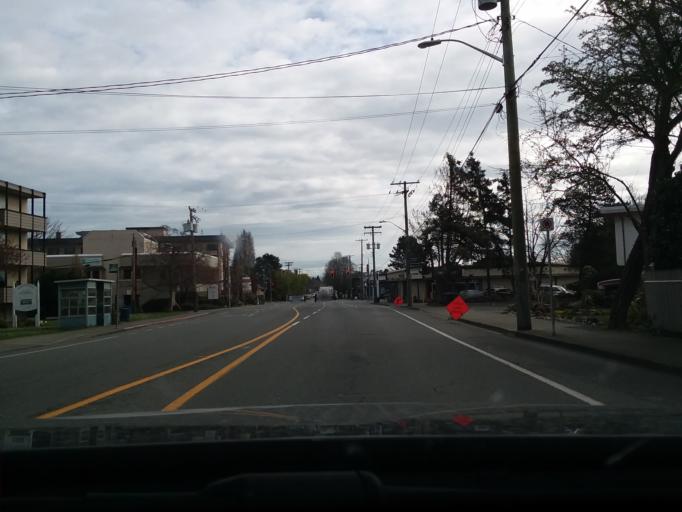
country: CA
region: British Columbia
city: Oak Bay
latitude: 48.4289
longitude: -123.3317
